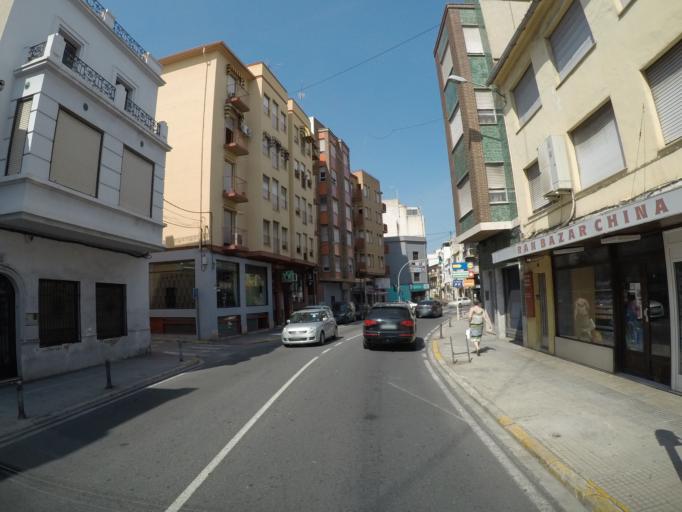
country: ES
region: Valencia
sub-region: Provincia de Valencia
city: Oliva
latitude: 38.9184
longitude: -0.1179
